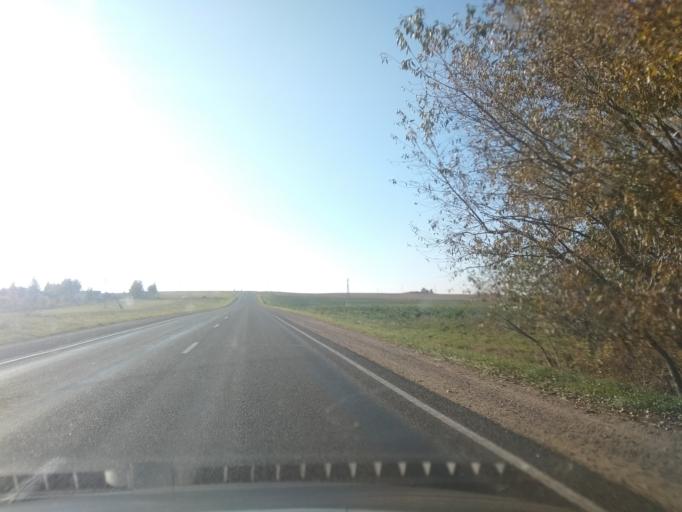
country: BY
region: Grodnenskaya
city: Svislach
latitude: 53.1321
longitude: 24.1992
